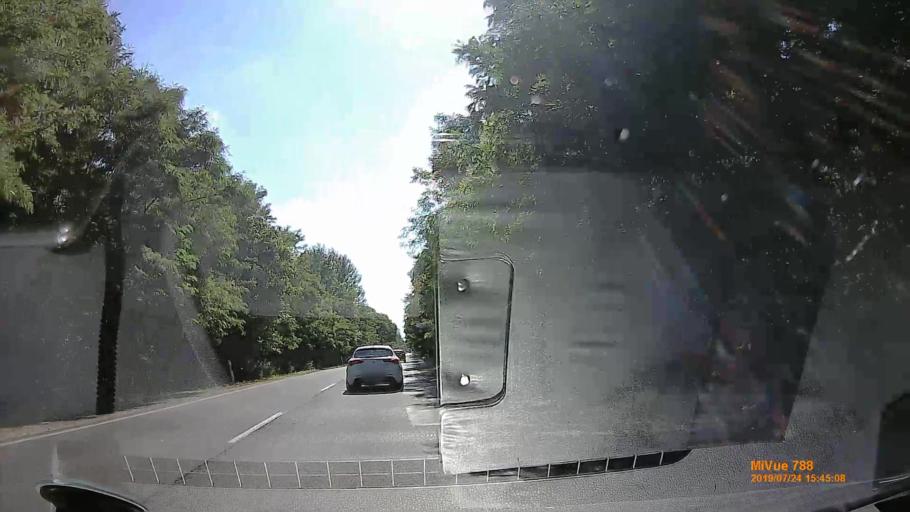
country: HU
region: Szabolcs-Szatmar-Bereg
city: Nagydobos
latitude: 48.0921
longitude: 22.2846
